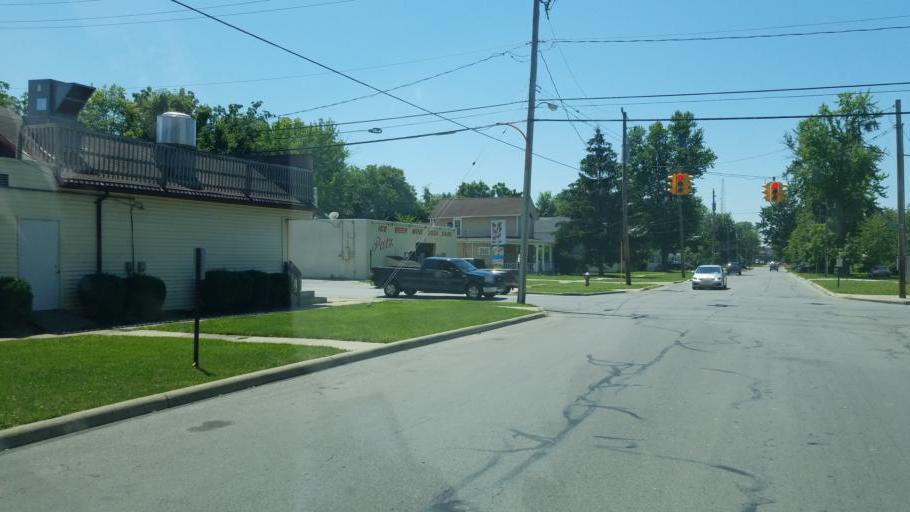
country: US
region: Ohio
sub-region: Ottawa County
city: Port Clinton
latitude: 41.5106
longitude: -82.9334
